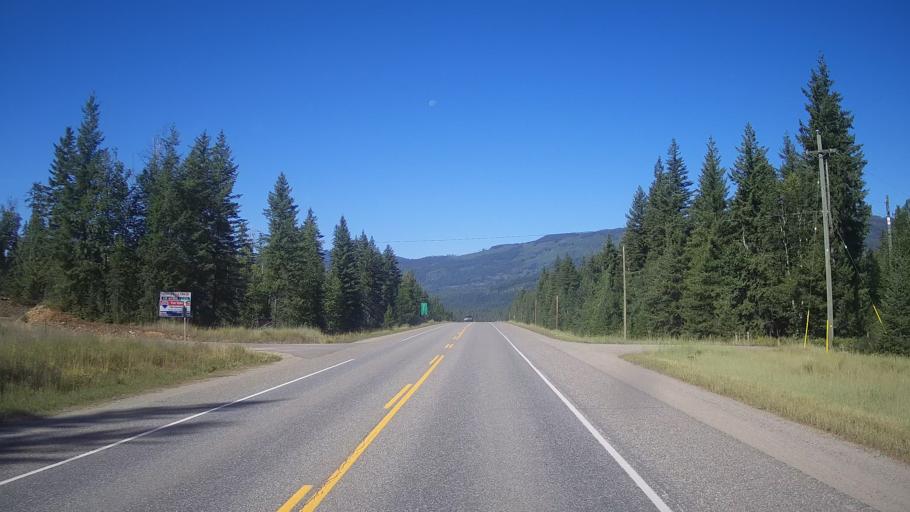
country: CA
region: British Columbia
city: Chase
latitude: 51.6420
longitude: -120.0645
